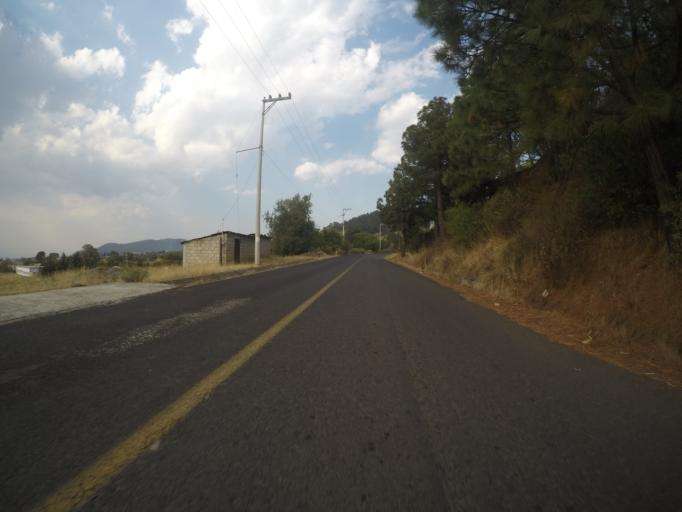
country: MX
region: Mexico
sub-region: Xalatlaco
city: San Juan Tomasquillo Herradura
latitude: 19.1648
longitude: -99.3938
